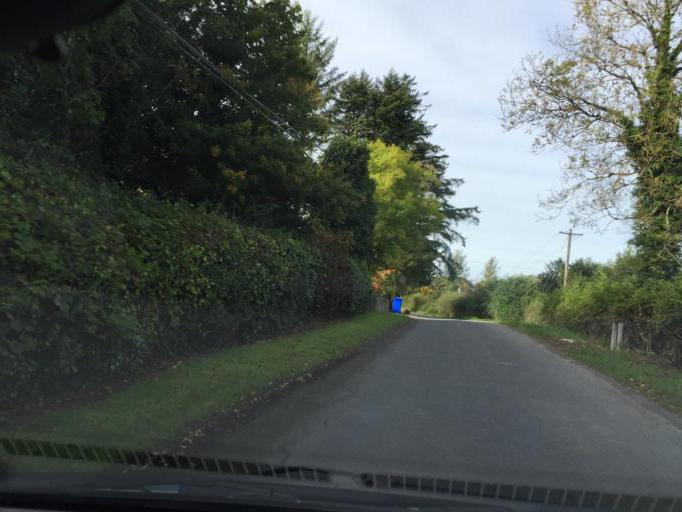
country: IE
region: Connaught
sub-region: Roscommon
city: Boyle
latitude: 54.0298
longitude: -8.2892
